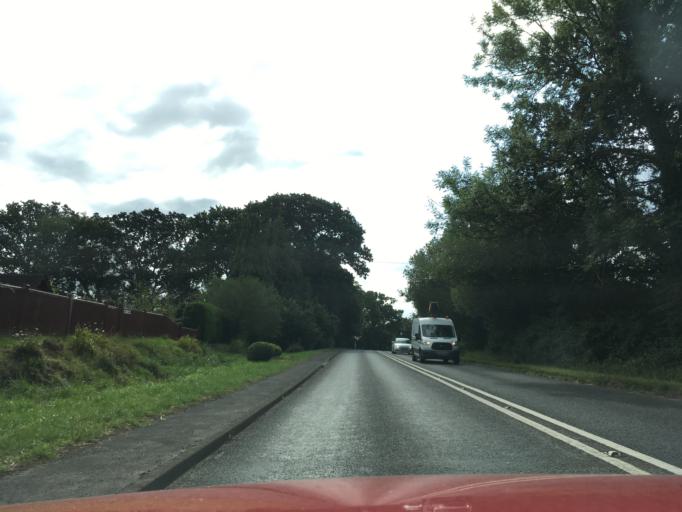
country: GB
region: England
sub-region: Hampshire
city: Bishops Waltham
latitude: 50.9692
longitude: -1.2488
